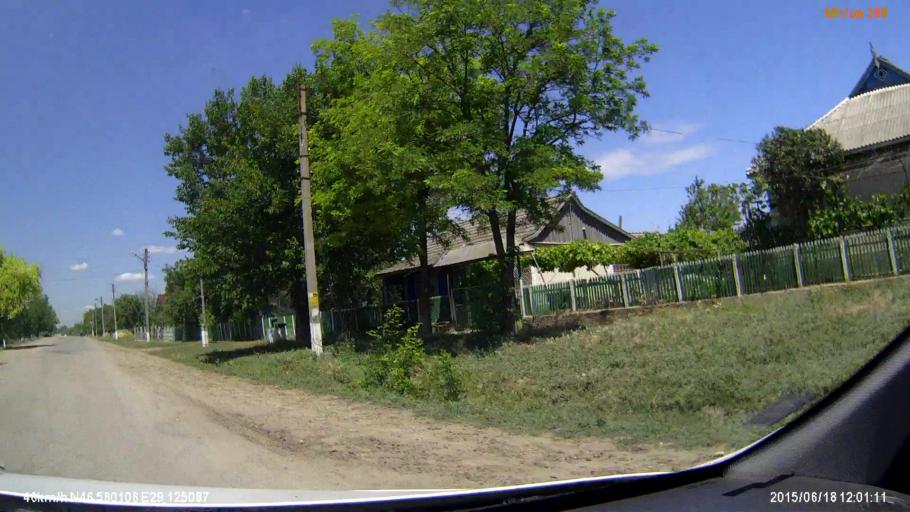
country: MD
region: Basarabeasca
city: Basarabeasca
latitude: 46.5599
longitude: 29.1253
